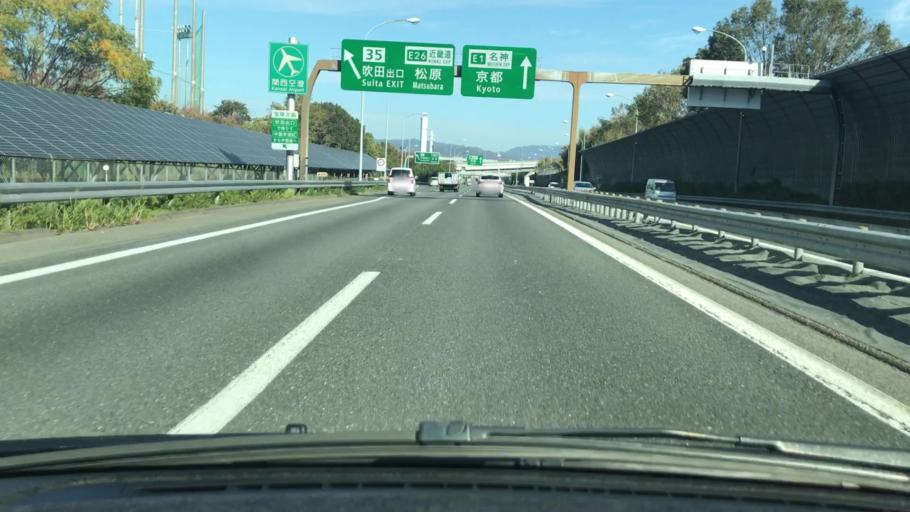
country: JP
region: Osaka
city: Ibaraki
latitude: 34.7995
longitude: 135.5397
